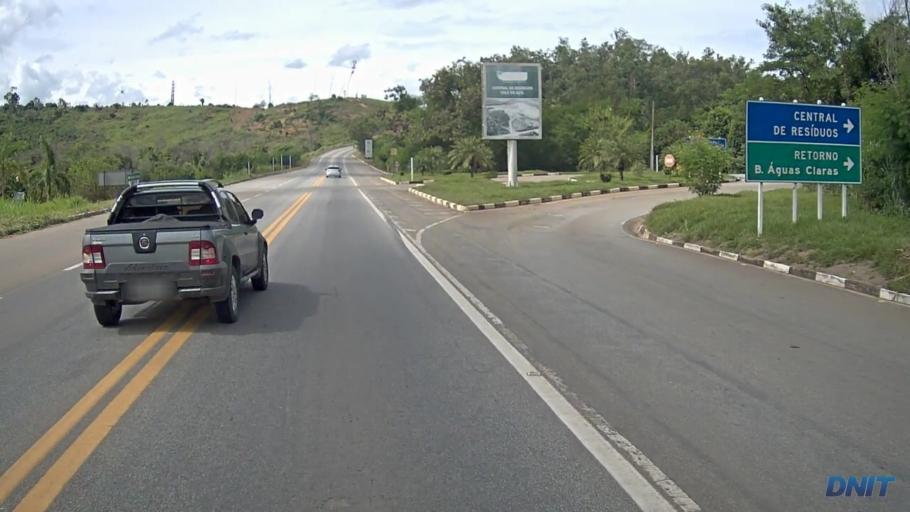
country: BR
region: Minas Gerais
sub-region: Ipatinga
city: Ipatinga
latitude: -19.4392
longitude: -42.5111
